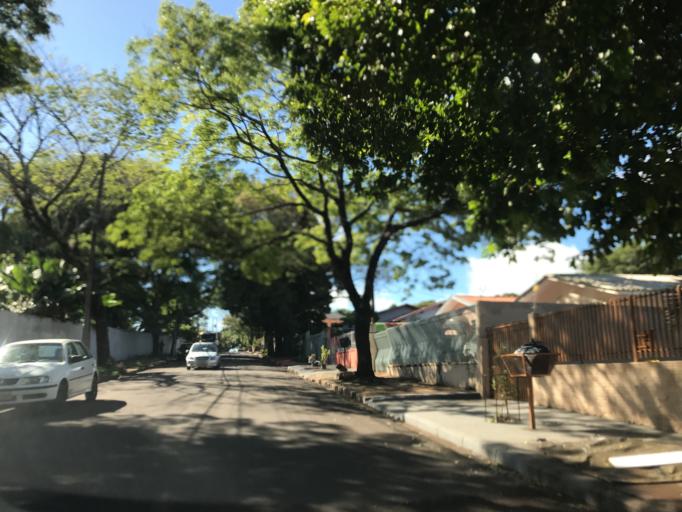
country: BR
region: Parana
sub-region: Maringa
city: Maringa
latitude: -23.4524
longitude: -51.9607
